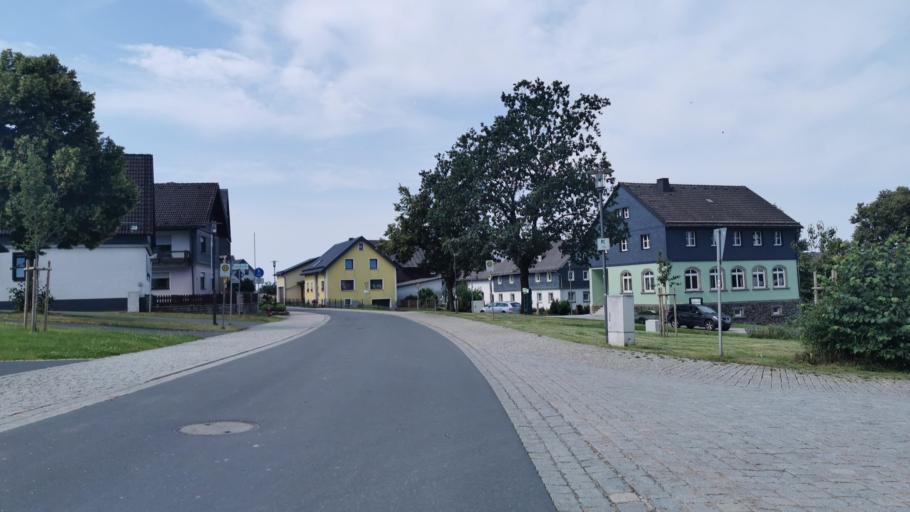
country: DE
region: Bavaria
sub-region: Upper Franconia
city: Steinwiesen
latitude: 50.3324
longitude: 11.4267
